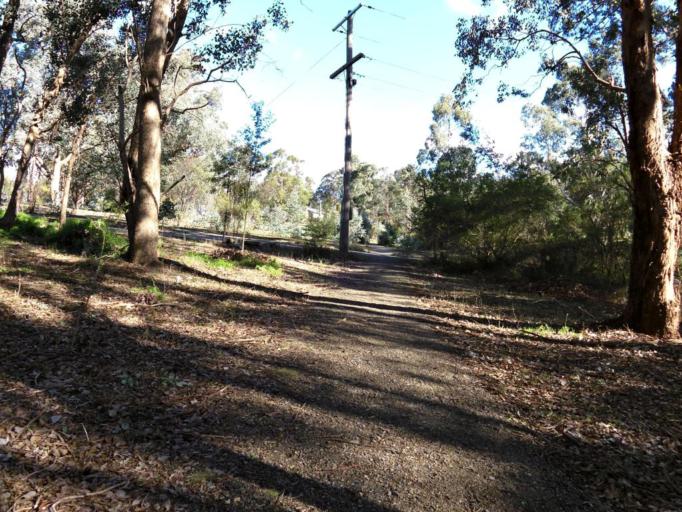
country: AU
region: Victoria
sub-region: Nillumbik
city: North Warrandyte
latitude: -37.7334
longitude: 145.2096
